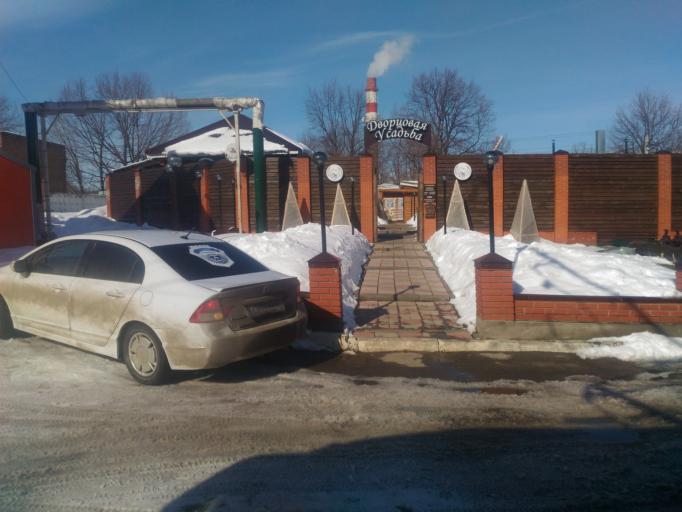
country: RU
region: Ulyanovsk
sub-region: Ulyanovskiy Rayon
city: Ulyanovsk
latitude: 54.3501
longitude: 48.3515
